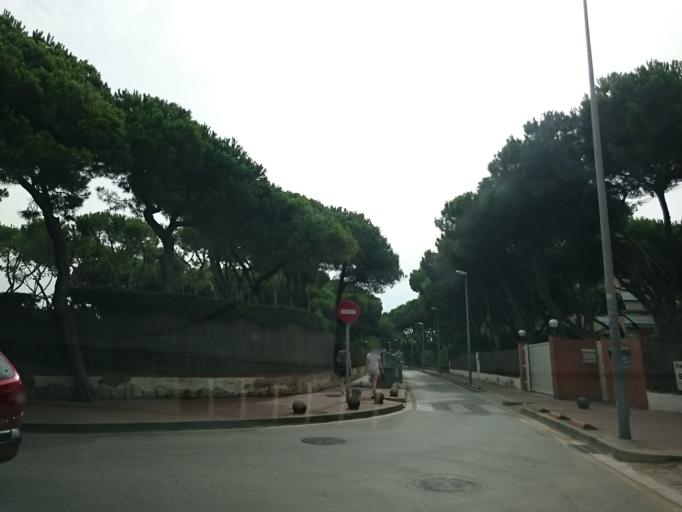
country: ES
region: Catalonia
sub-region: Provincia de Barcelona
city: Gava
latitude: 41.2683
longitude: 2.0264
